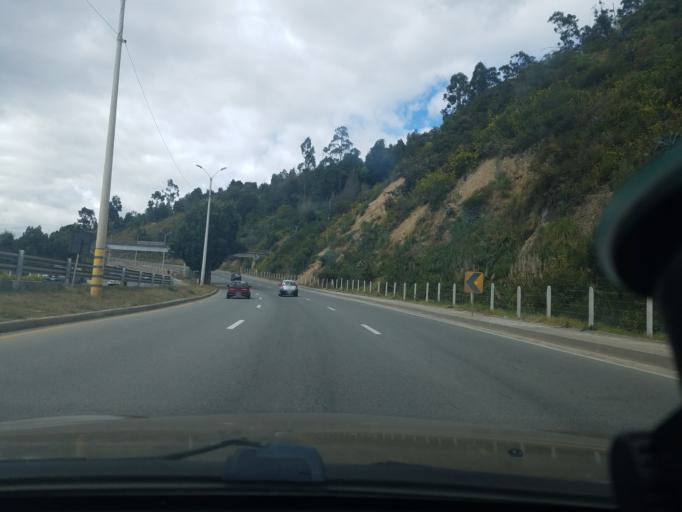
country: EC
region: Azuay
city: Llacao
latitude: -2.8636
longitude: -78.9303
